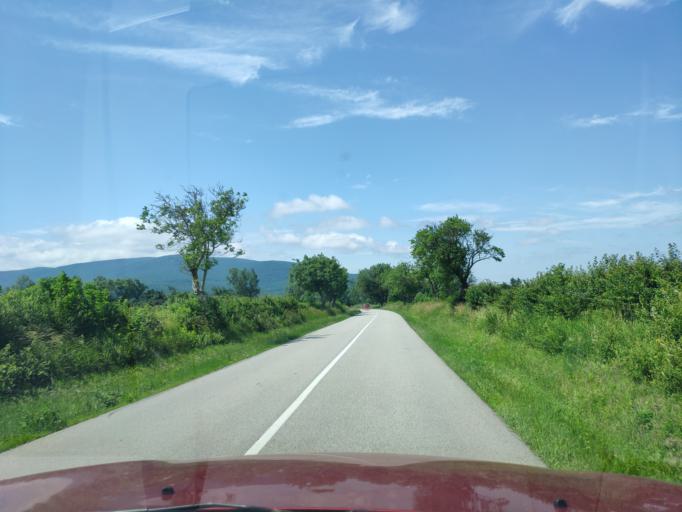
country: SK
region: Kosicky
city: Secovce
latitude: 48.7397
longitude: 21.6490
